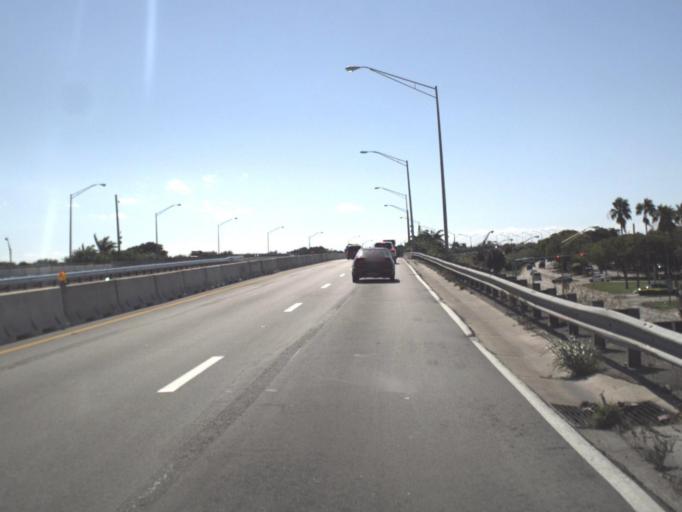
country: US
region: Florida
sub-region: Miami-Dade County
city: Cutler Ridge
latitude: 25.5740
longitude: -80.3641
